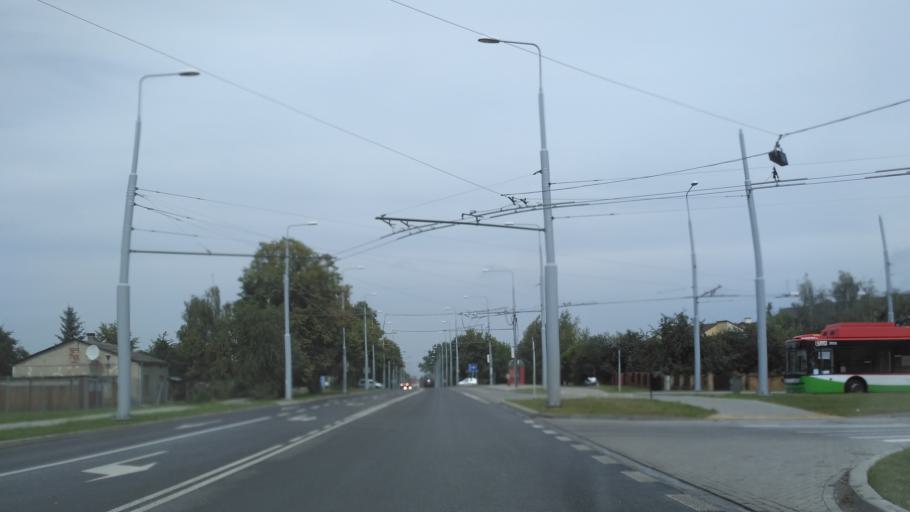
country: PL
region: Lublin Voivodeship
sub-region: Powiat lubelski
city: Lublin
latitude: 51.1966
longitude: 22.5860
